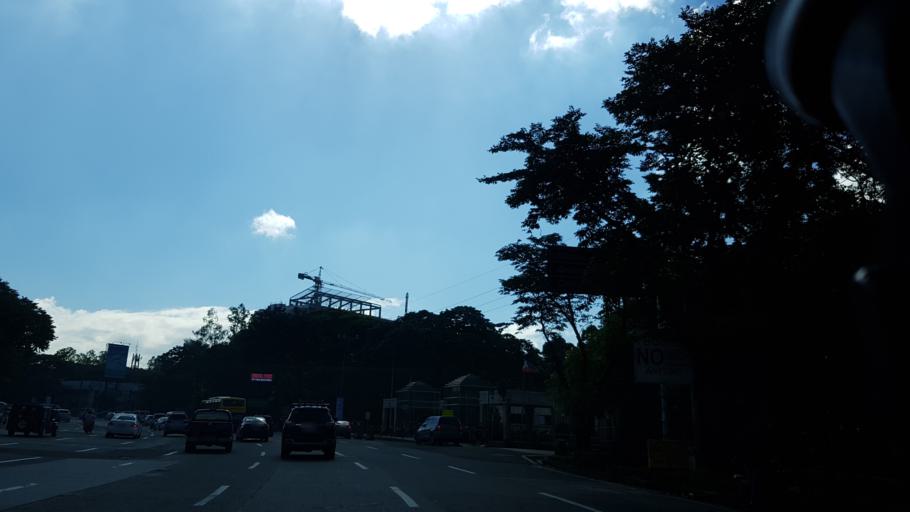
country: PH
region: Metro Manila
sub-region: Quezon City
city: Quezon City
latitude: 14.6485
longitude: 121.0493
